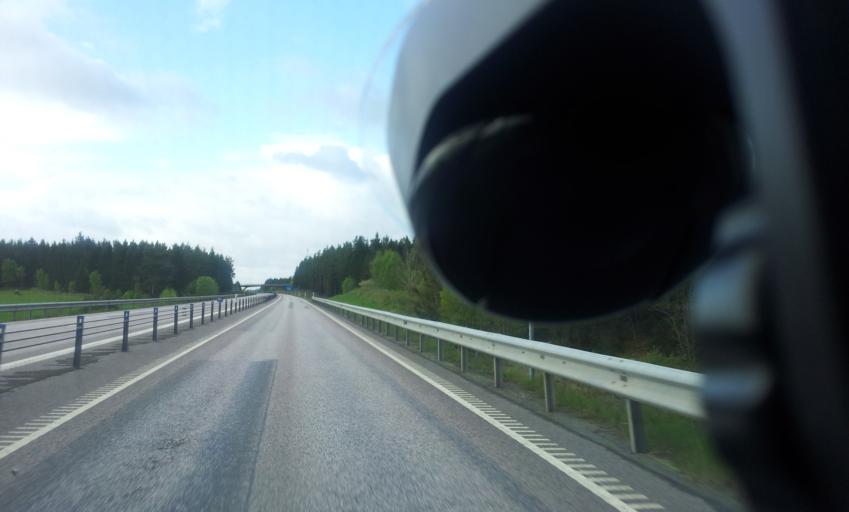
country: SE
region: Kalmar
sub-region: Torsas Kommun
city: Torsas
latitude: 56.4698
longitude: 16.0801
